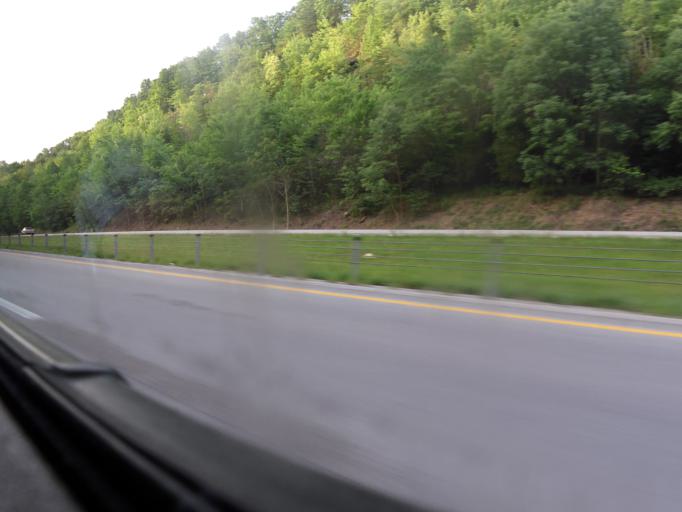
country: US
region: Kentucky
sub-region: Rockcastle County
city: Mount Vernon
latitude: 37.3283
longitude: -84.3034
